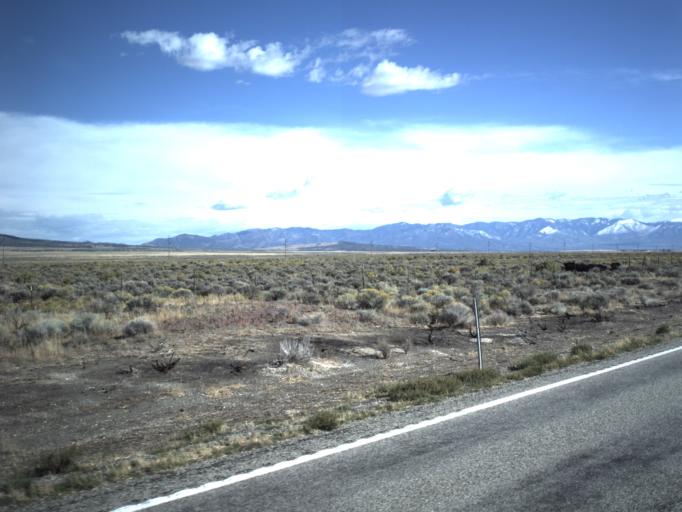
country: US
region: Utah
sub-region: Millard County
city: Delta
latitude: 39.2706
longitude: -112.4541
